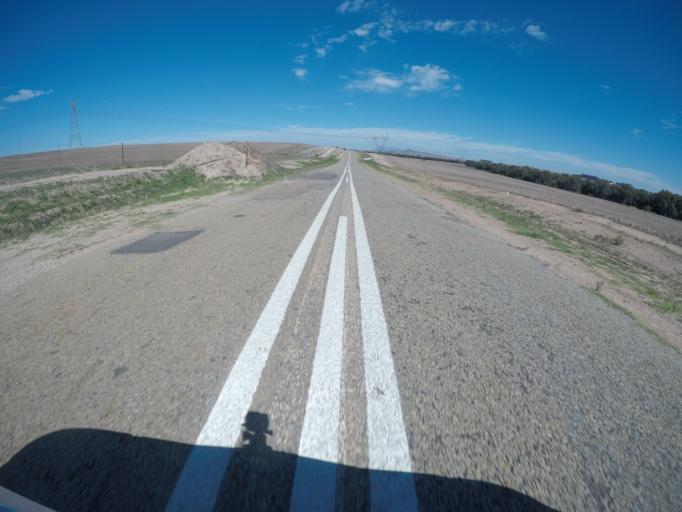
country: ZA
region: Western Cape
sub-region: West Coast District Municipality
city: Malmesbury
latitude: -33.5950
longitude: 18.6439
